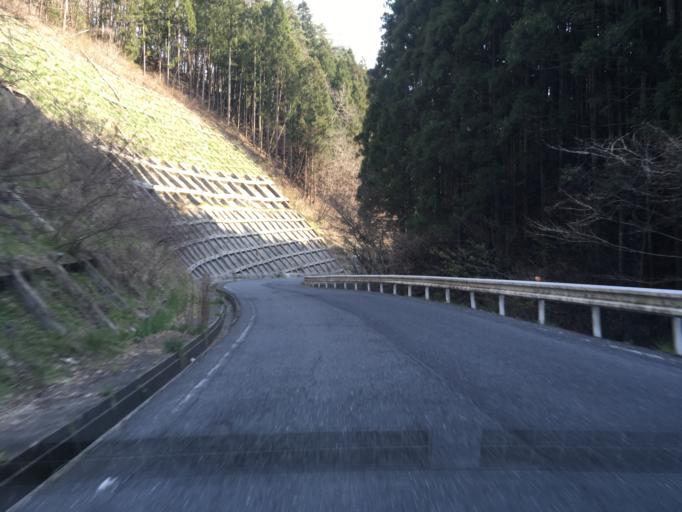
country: JP
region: Iwate
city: Ichinoseki
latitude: 38.8141
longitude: 141.3144
